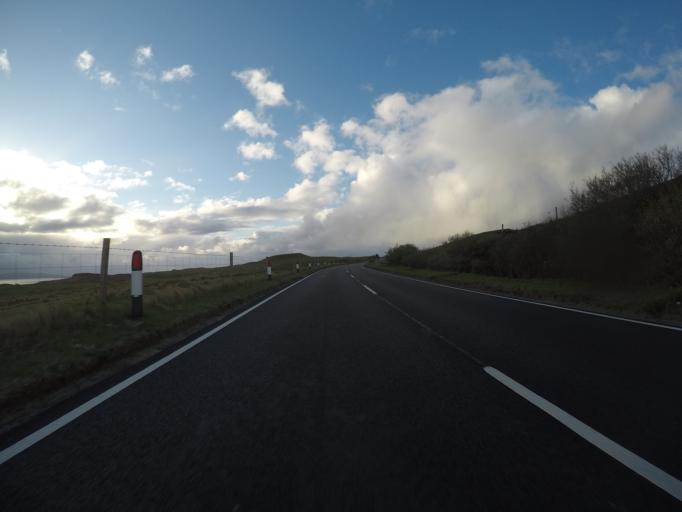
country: GB
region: Scotland
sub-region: Highland
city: Portree
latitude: 57.5419
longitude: -6.3646
